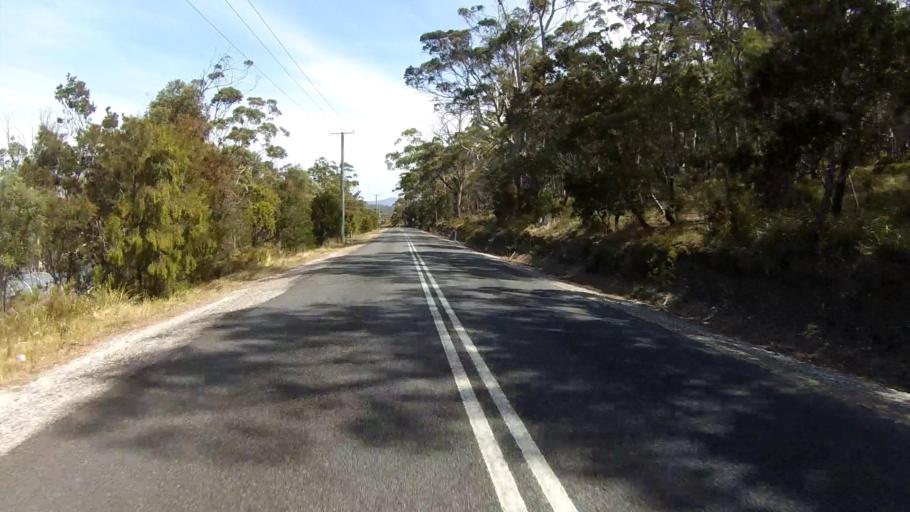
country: AU
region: Tasmania
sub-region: Huon Valley
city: Cygnet
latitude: -43.2734
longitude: 147.1503
